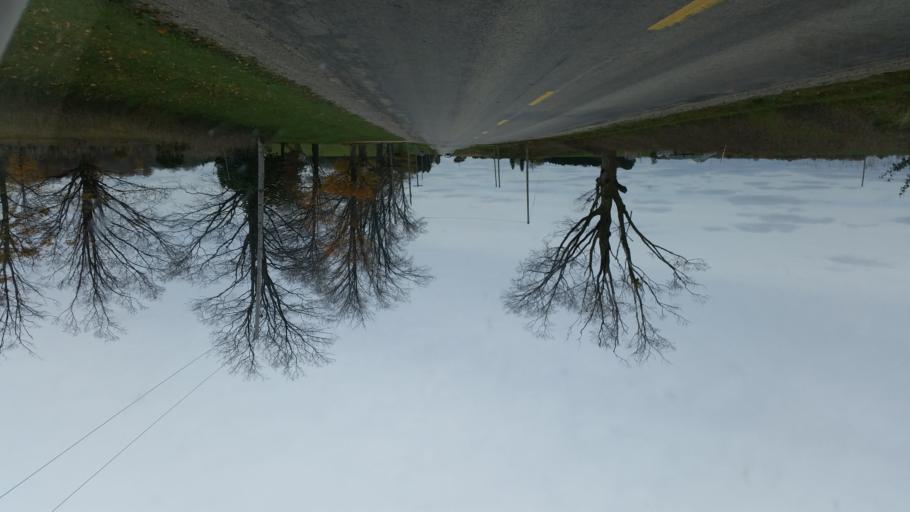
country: CA
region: Ontario
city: Wingham
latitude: 43.9953
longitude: -81.3244
